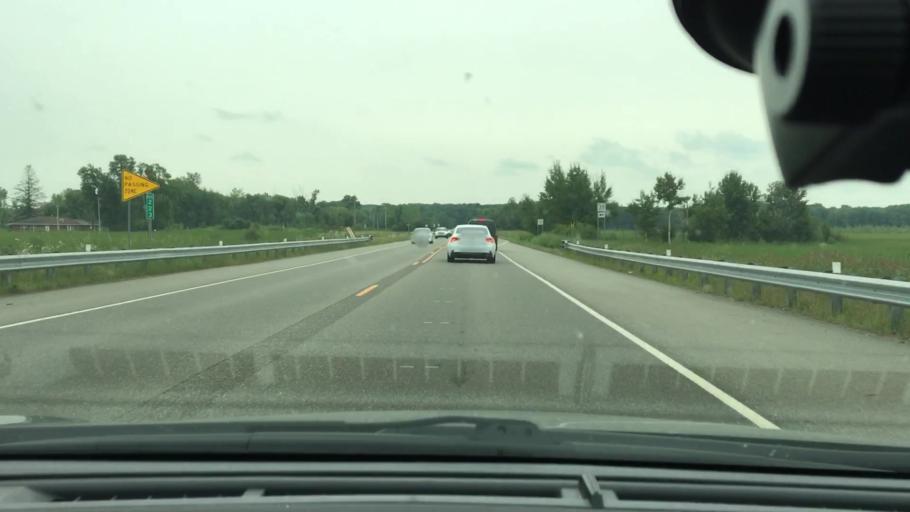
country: US
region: Minnesota
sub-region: Mille Lacs County
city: Vineland
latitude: 46.1597
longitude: -93.7578
